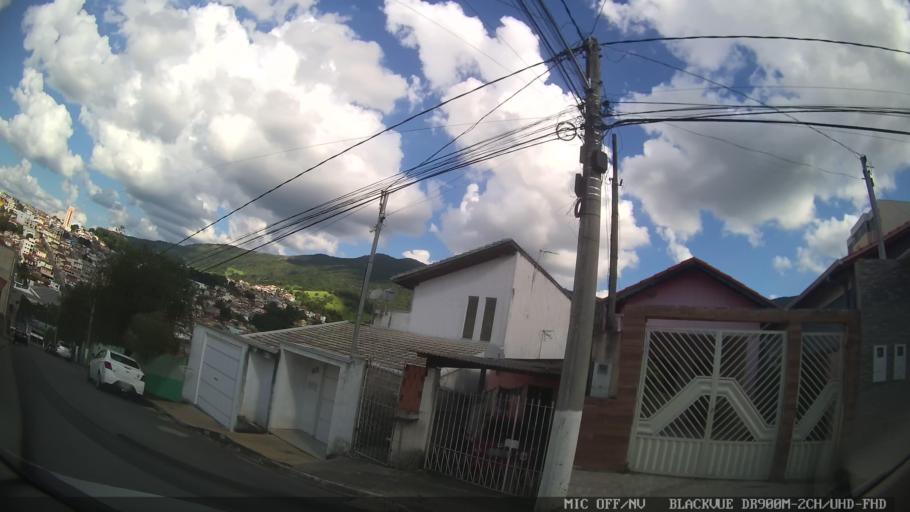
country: BR
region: Minas Gerais
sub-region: Extrema
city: Extrema
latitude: -22.8588
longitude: -46.3261
